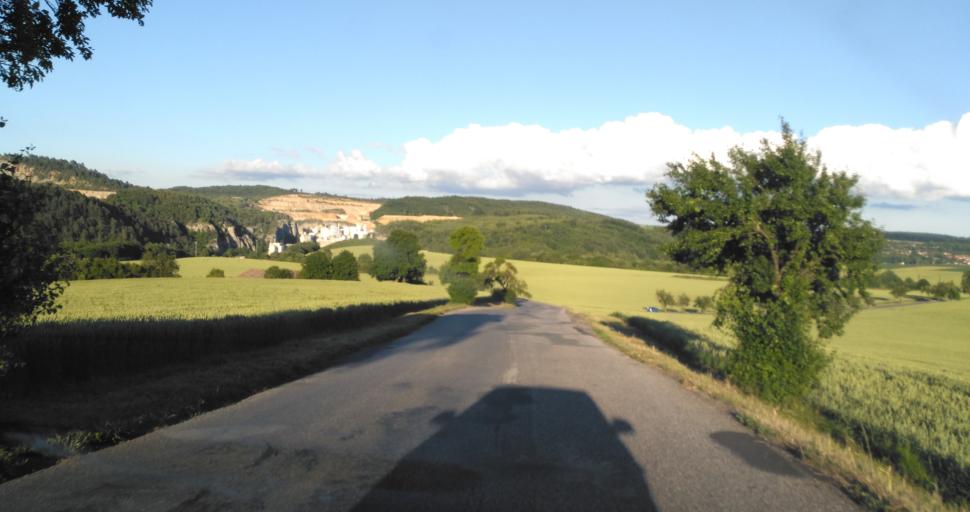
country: CZ
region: Central Bohemia
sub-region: Okres Beroun
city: Kraluv Dvur
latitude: 49.9122
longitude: 14.0377
